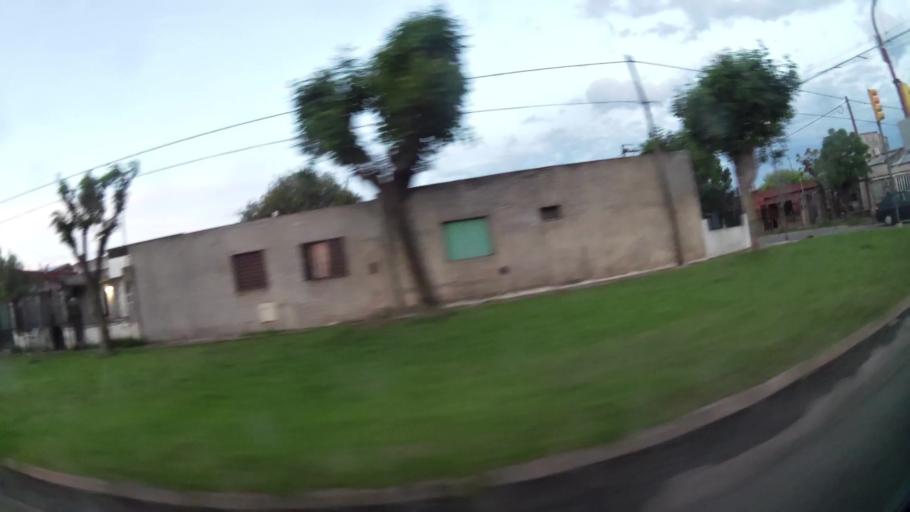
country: AR
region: Buenos Aires
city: San Nicolas de los Arroyos
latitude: -33.3565
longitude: -60.2077
